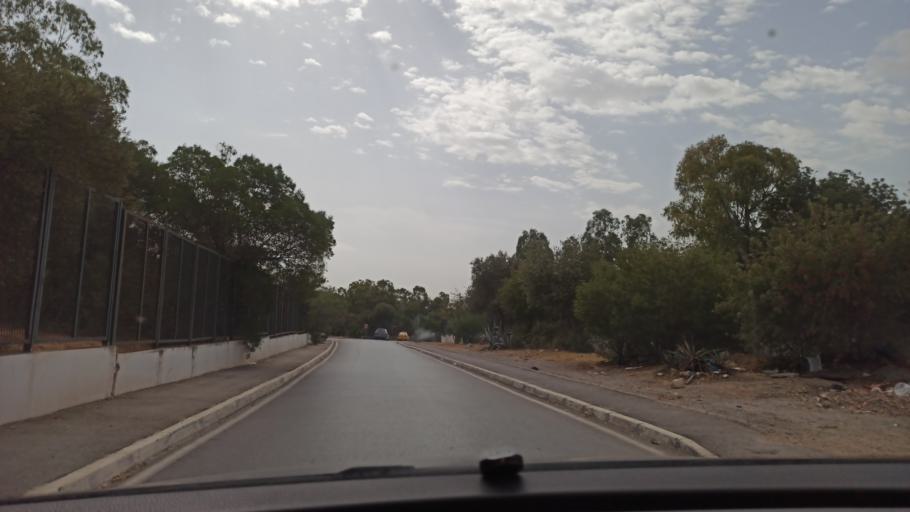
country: TN
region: Tunis
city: Tunis
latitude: 36.8208
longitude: 10.1682
